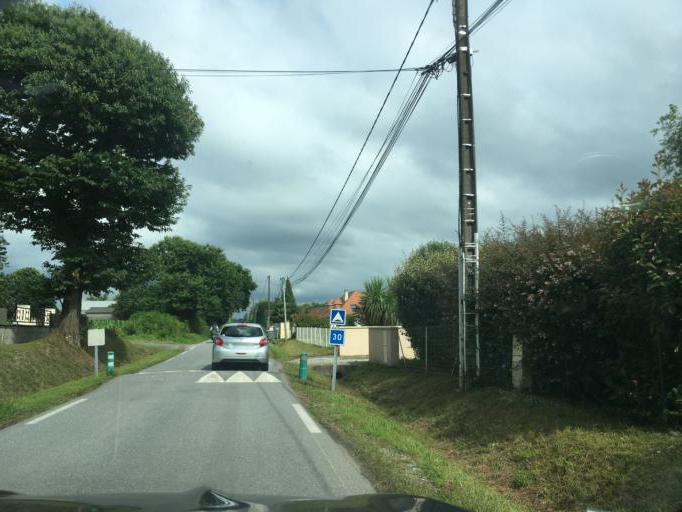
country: FR
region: Aquitaine
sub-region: Departement des Pyrenees-Atlantiques
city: Ousse
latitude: 43.3128
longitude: -0.2819
